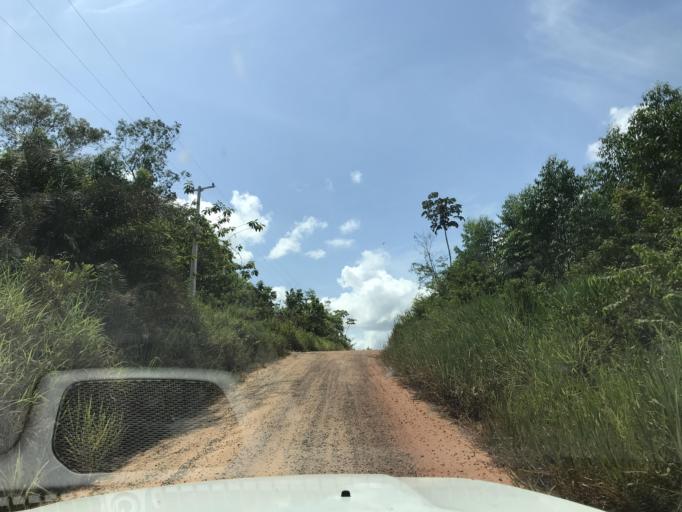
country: BR
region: Bahia
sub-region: Entre Rios
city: Entre Rios
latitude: -12.2166
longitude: -38.0777
